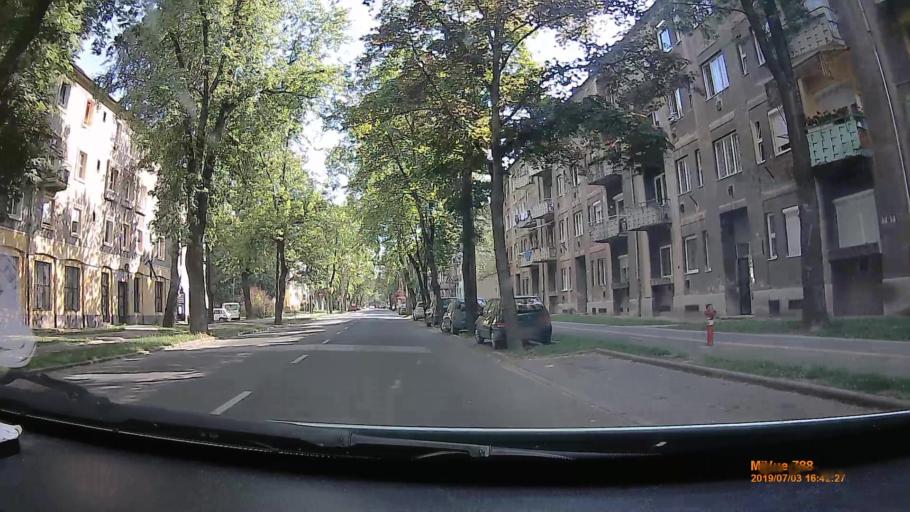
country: HU
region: Borsod-Abauj-Zemplen
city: Kazincbarcika
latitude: 48.2529
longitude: 20.6191
